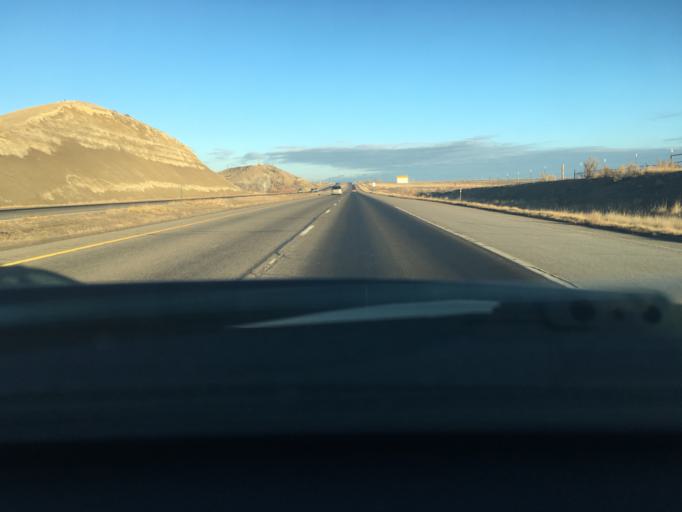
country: US
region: Colorado
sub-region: Montrose County
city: Olathe
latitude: 38.5353
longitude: -107.9387
